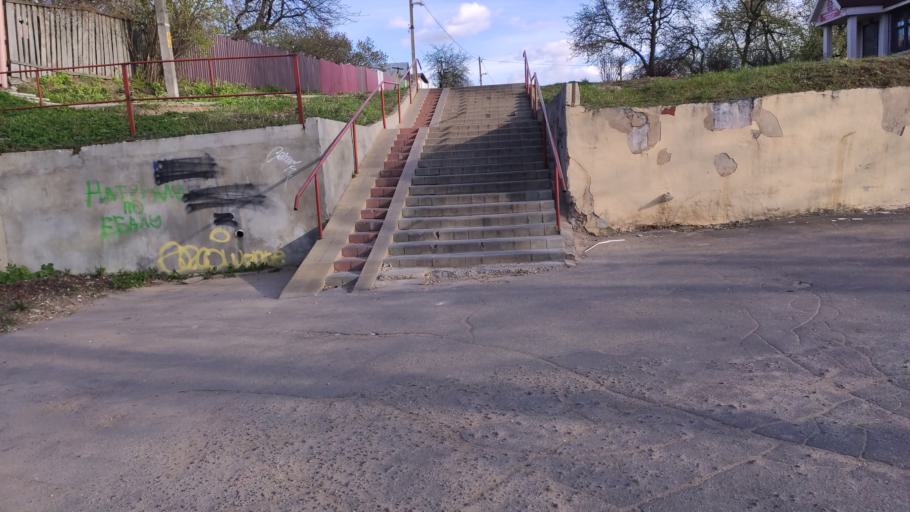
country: BY
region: Minsk
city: Minsk
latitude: 53.8998
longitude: 27.5171
